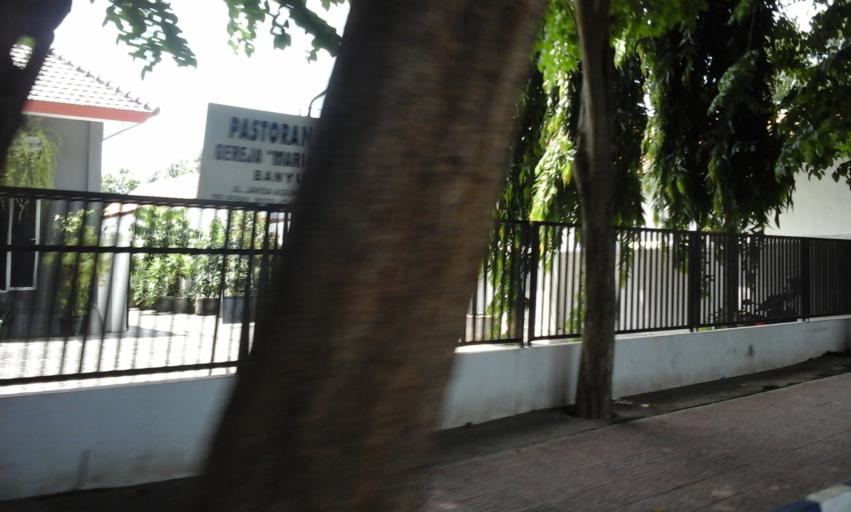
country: ID
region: East Java
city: Wirodayan
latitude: -8.2162
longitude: 114.3676
